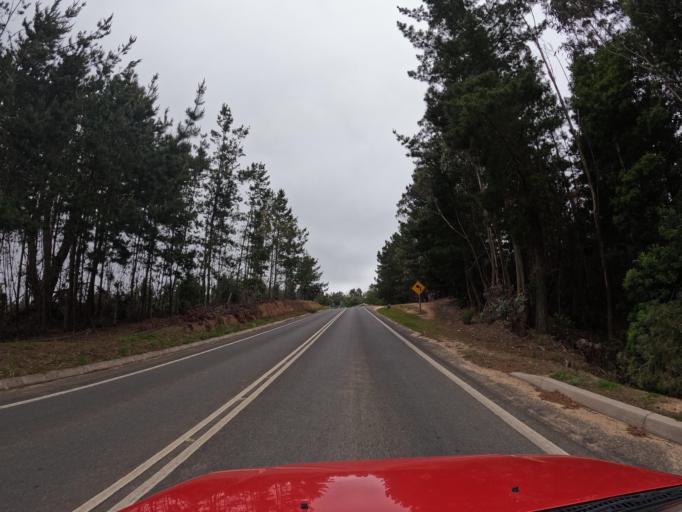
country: CL
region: O'Higgins
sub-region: Provincia de Colchagua
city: Santa Cruz
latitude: -34.6169
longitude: -72.0129
